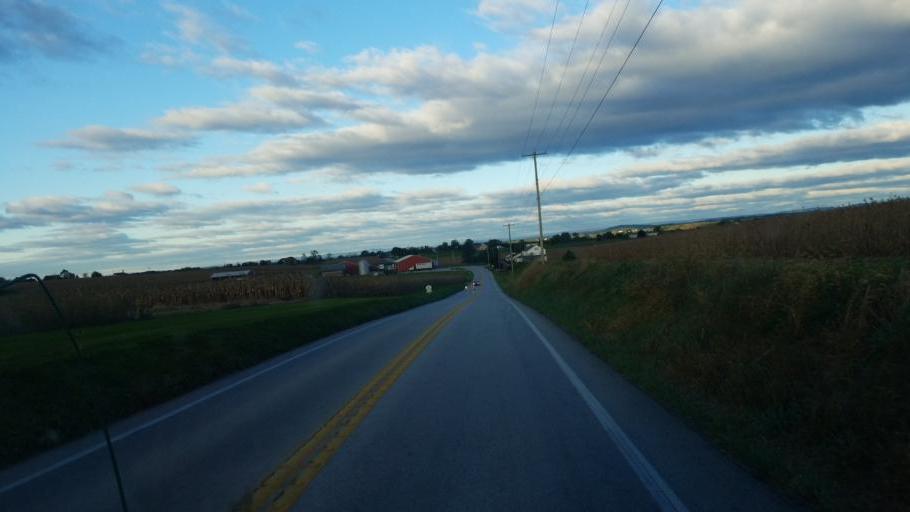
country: US
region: Pennsylvania
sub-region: Adams County
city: East Berlin
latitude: 39.9368
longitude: -76.9487
